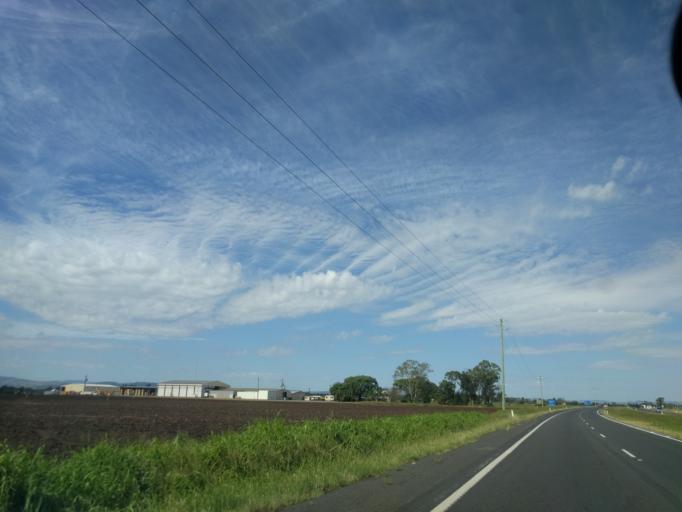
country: AU
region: Queensland
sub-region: Lockyer Valley
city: Gatton
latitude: -27.5431
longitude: 152.3546
